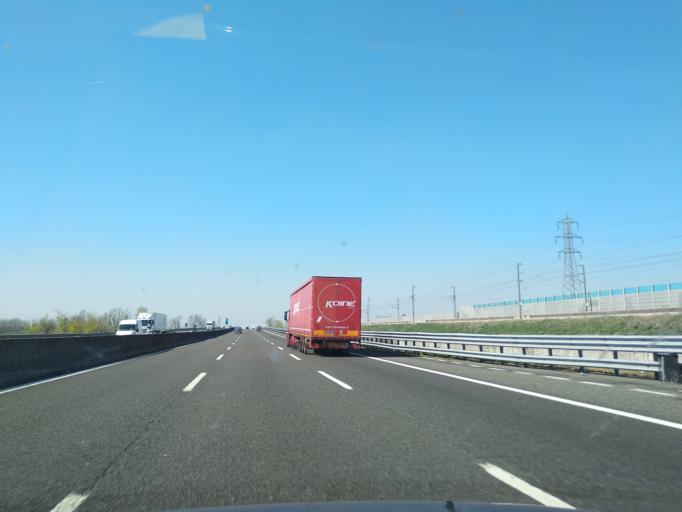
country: IT
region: Emilia-Romagna
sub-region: Provincia di Reggio Emilia
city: Massenzatico
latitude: 44.7183
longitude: 10.6816
